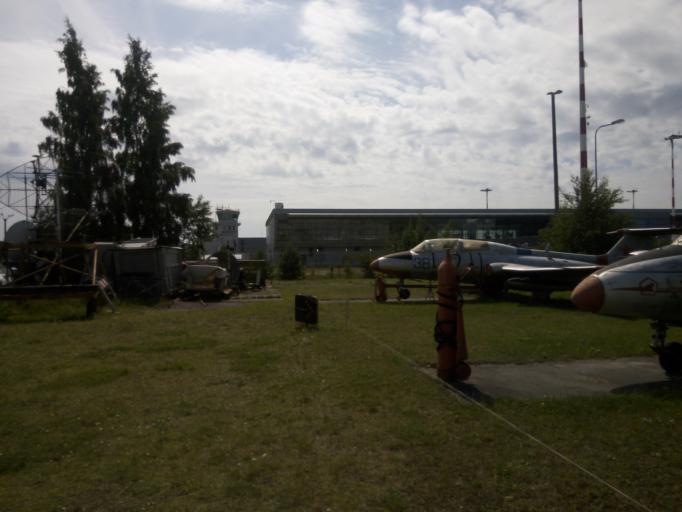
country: LV
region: Babite
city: Pinki
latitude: 56.9259
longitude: 23.9801
